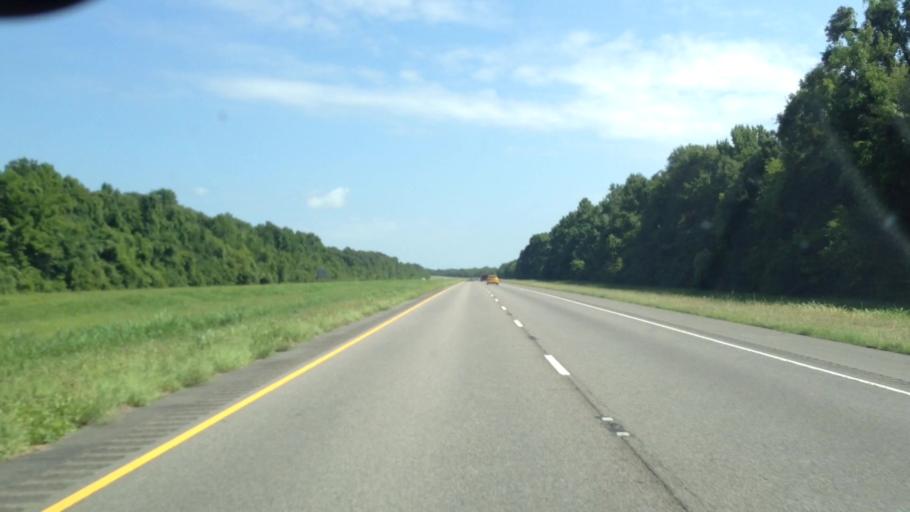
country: US
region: Louisiana
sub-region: Avoyelles Parish
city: Bunkie
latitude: 30.8828
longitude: -92.2270
